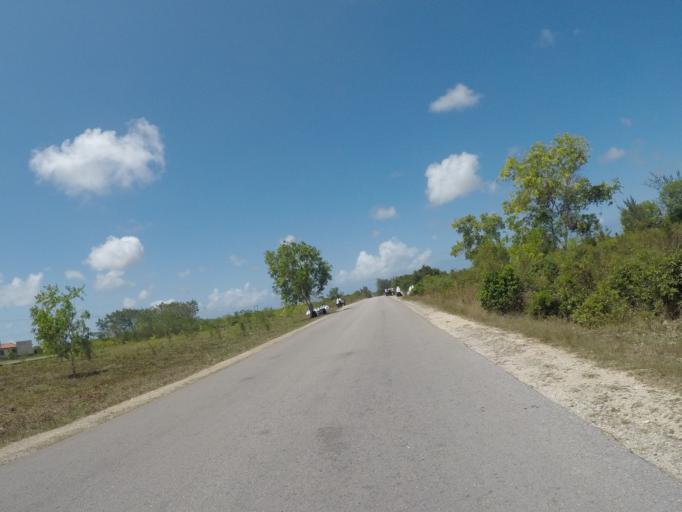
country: TZ
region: Zanzibar Central/South
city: Nganane
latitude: -6.2819
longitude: 39.4721
